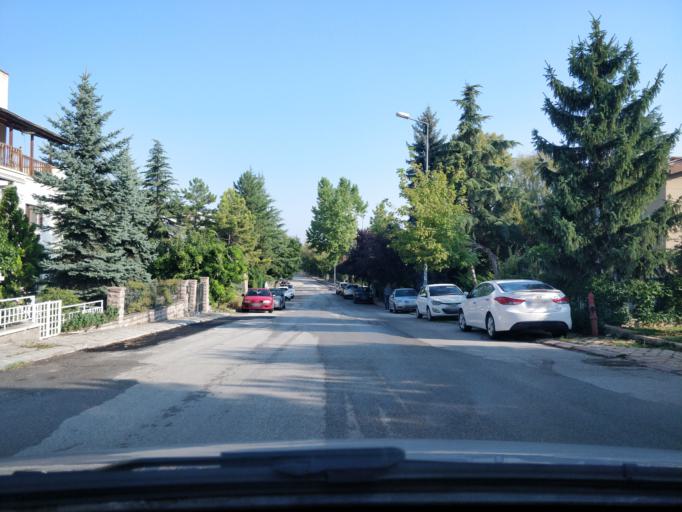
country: TR
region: Ankara
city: Batikent
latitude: 39.8950
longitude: 32.7266
